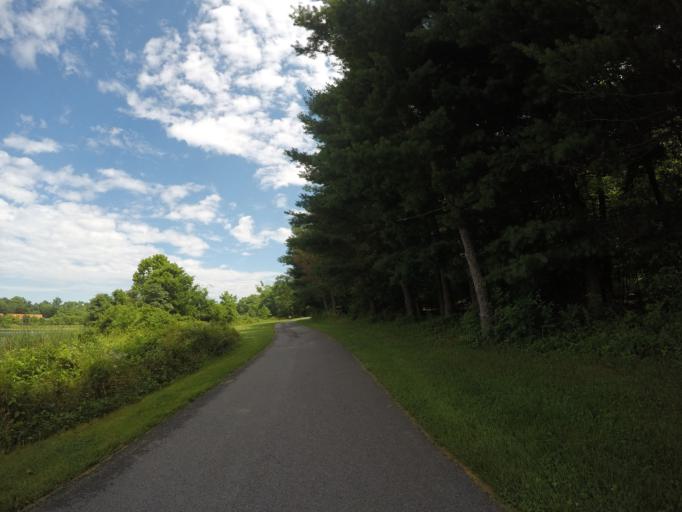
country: US
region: Maryland
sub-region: Prince George's County
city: Berwyn Heights
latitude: 38.9892
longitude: -76.9213
